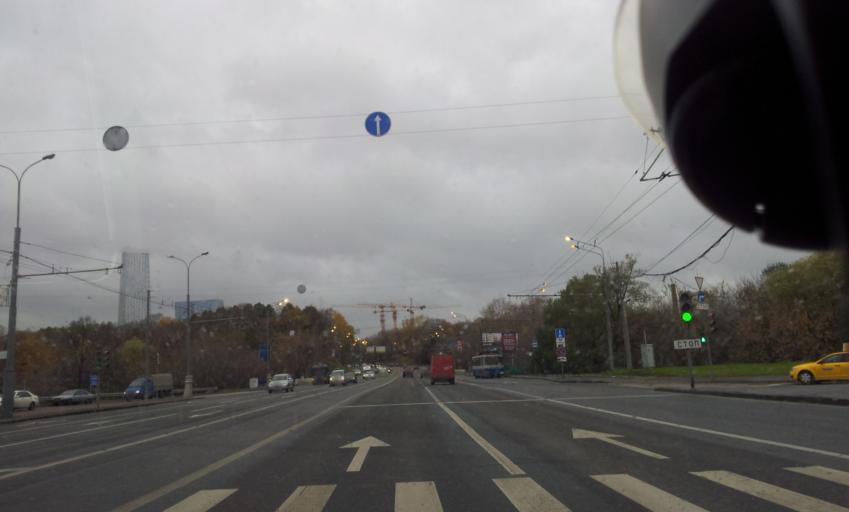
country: RU
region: Moscow
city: Luzhniki
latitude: 55.7286
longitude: 37.5460
